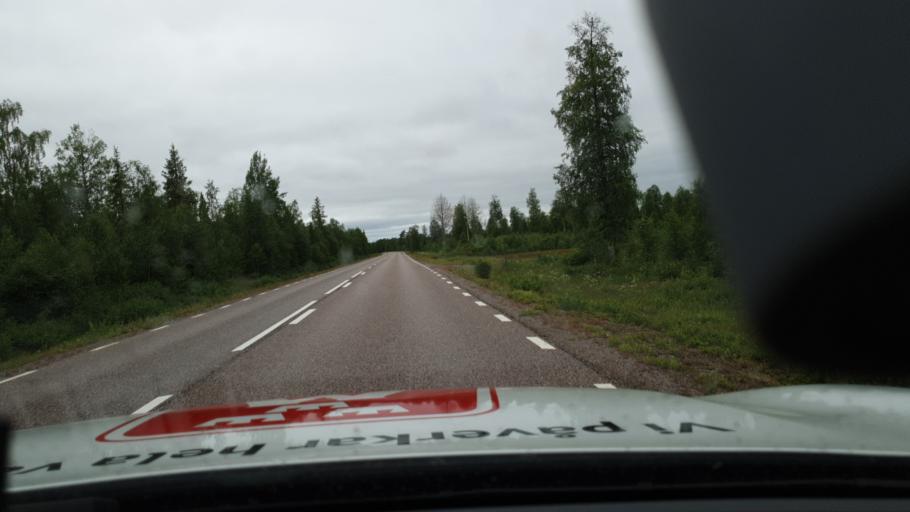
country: SE
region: Norrbotten
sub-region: Pajala Kommun
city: Pajala
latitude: 67.1972
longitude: 23.4478
